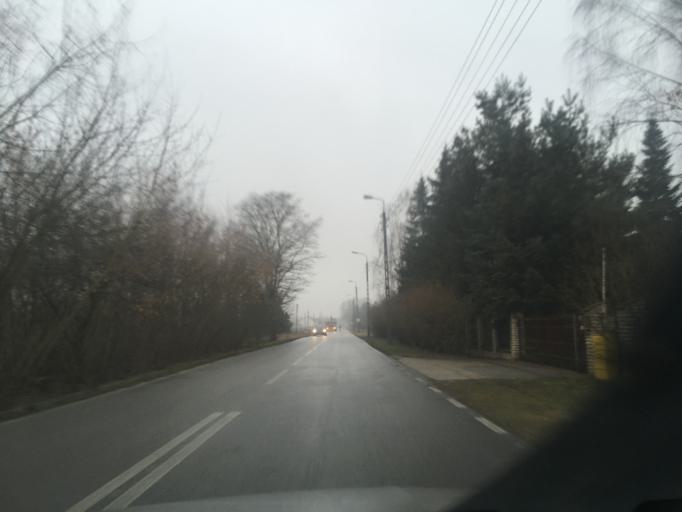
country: PL
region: Masovian Voivodeship
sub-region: Powiat piaseczynski
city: Lesznowola
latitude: 52.0540
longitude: 20.9049
